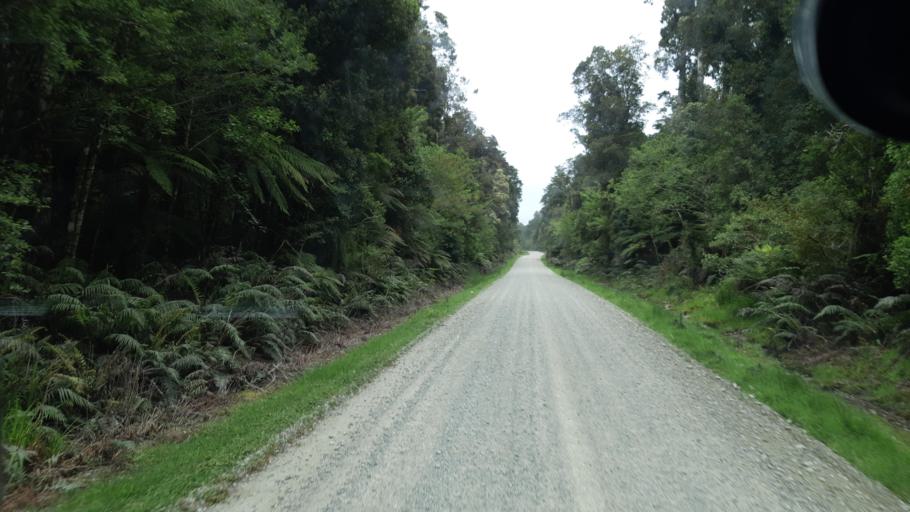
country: NZ
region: West Coast
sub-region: Grey District
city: Greymouth
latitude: -42.6469
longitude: 171.3335
